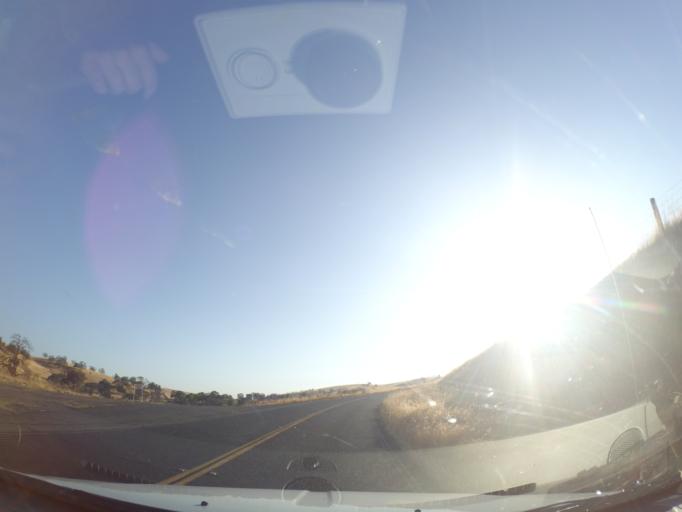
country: US
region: California
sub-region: Merced County
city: Planada
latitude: 37.4962
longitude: -120.2401
